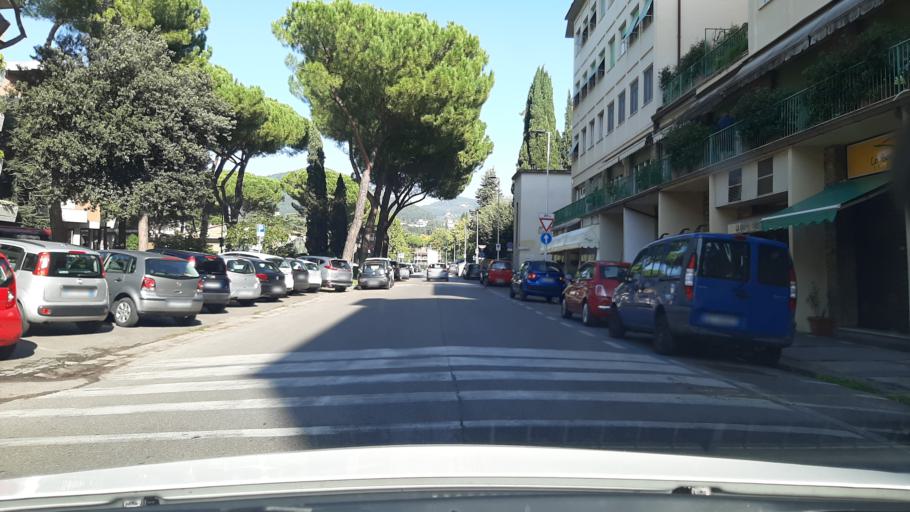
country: IT
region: Tuscany
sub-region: Province of Florence
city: Fiesole
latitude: 43.7802
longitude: 11.2919
